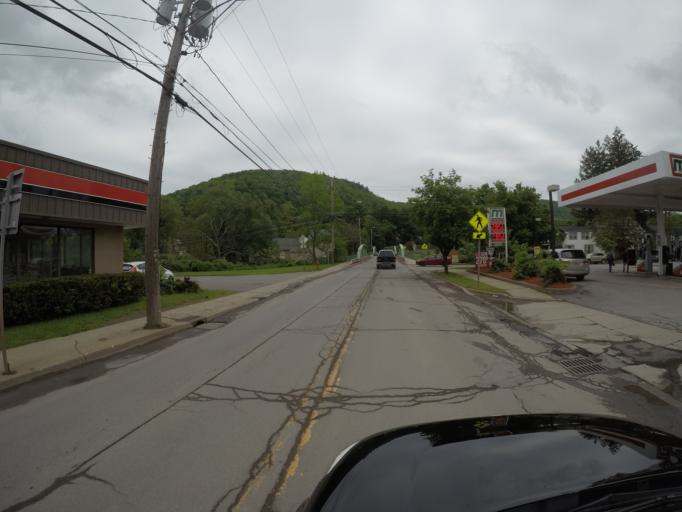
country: US
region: New York
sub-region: Delaware County
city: Delhi
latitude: 42.2756
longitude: -74.9173
